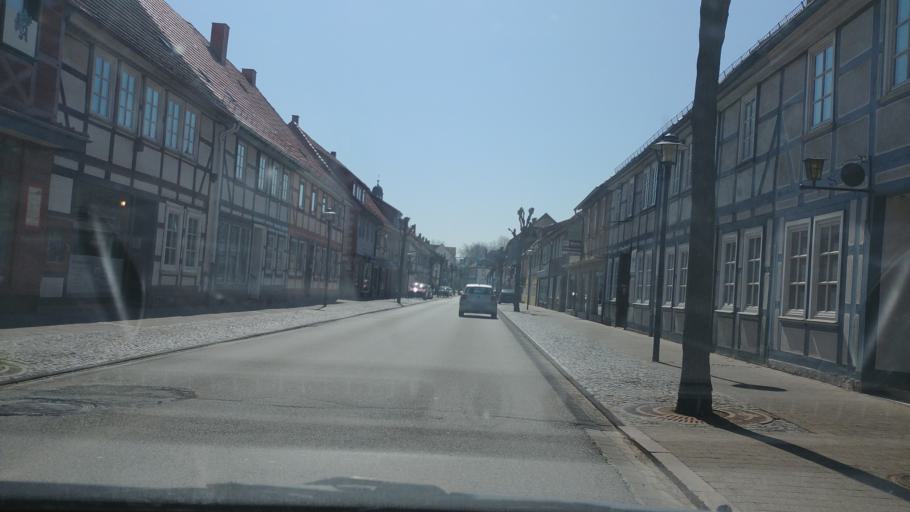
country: DE
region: Lower Saxony
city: Moringen
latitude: 51.7007
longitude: 9.8711
